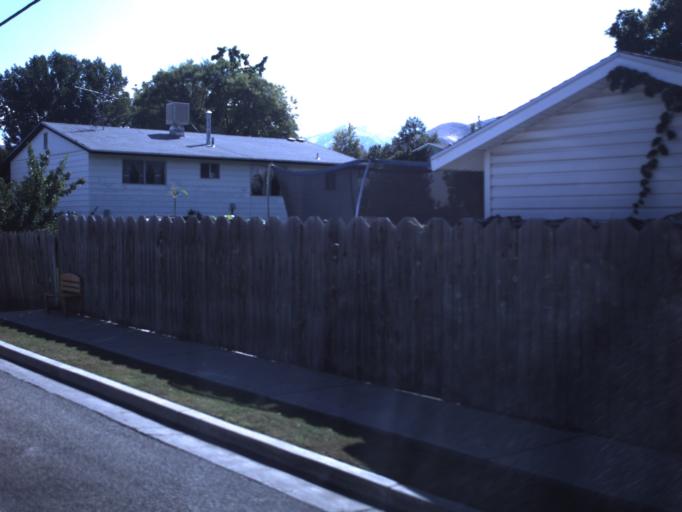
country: US
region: Utah
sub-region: Utah County
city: Payson
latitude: 40.0313
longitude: -111.7440
